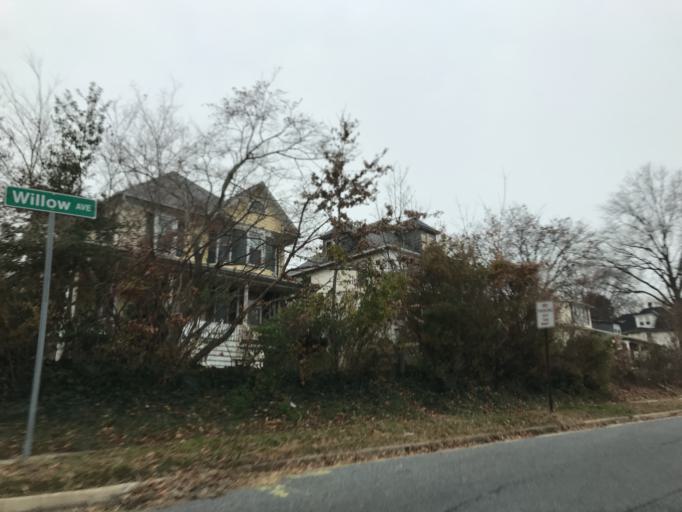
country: US
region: Maryland
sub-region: Baltimore County
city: Overlea
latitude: 39.3564
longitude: -76.5253
